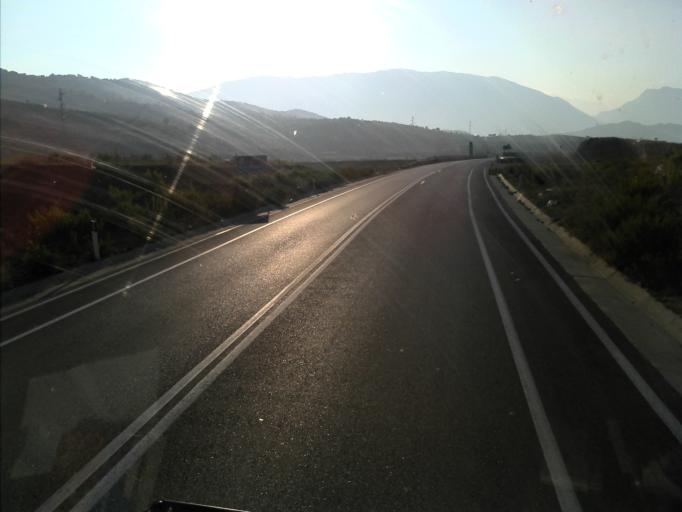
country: AL
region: Gjirokaster
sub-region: Rrethi i Tepelenes
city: Memaliaj
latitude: 40.3642
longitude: 19.9226
